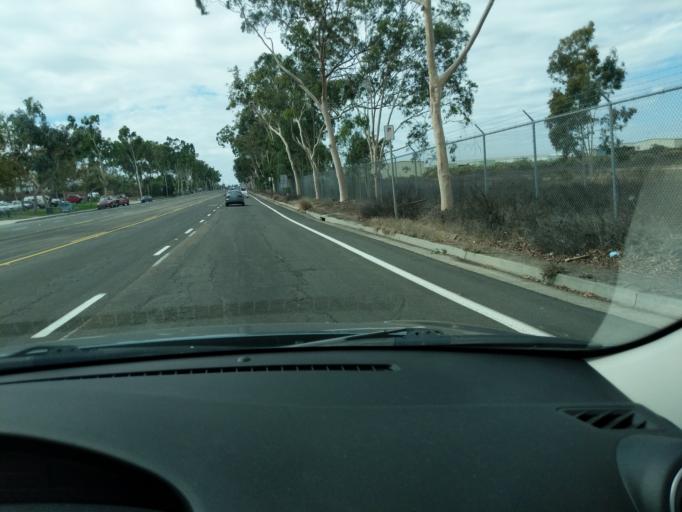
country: US
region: California
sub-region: San Diego County
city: San Diego
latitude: 32.8099
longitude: -117.1332
